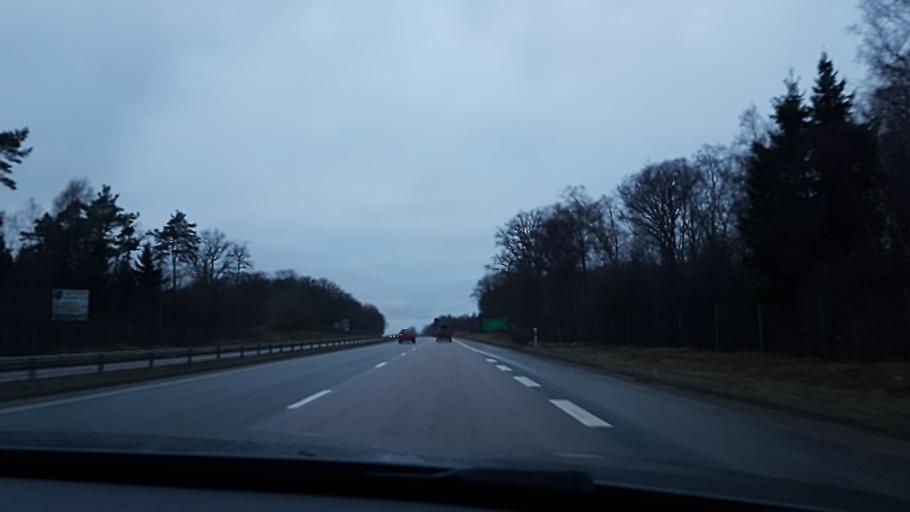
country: SE
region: Skane
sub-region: Astorps Kommun
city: Kvidinge
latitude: 56.2054
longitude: 13.0956
